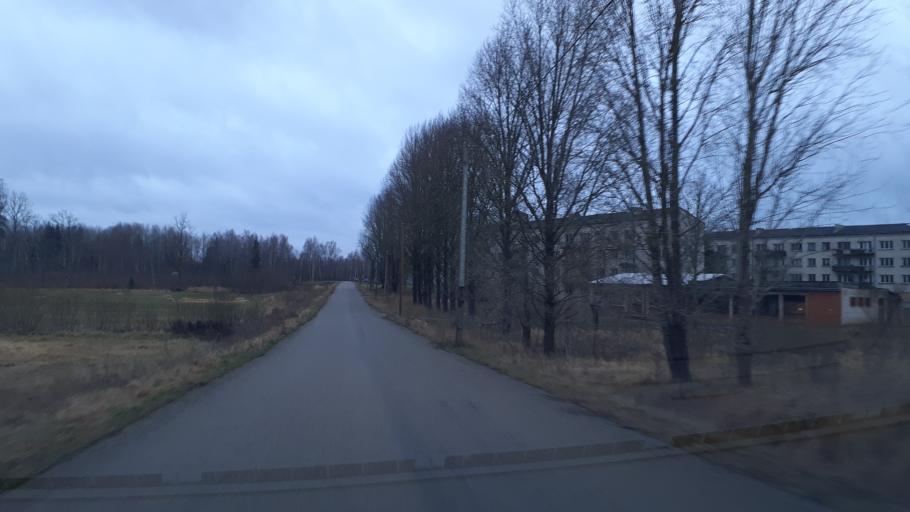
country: LV
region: Kuldigas Rajons
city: Kuldiga
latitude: 57.0419
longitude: 22.1294
